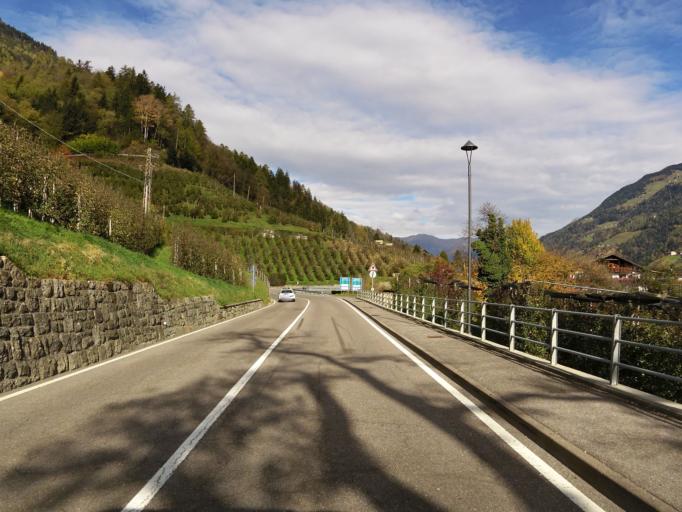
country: IT
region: Trentino-Alto Adige
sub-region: Bolzano
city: Rifiano
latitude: 46.7124
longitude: 11.1883
